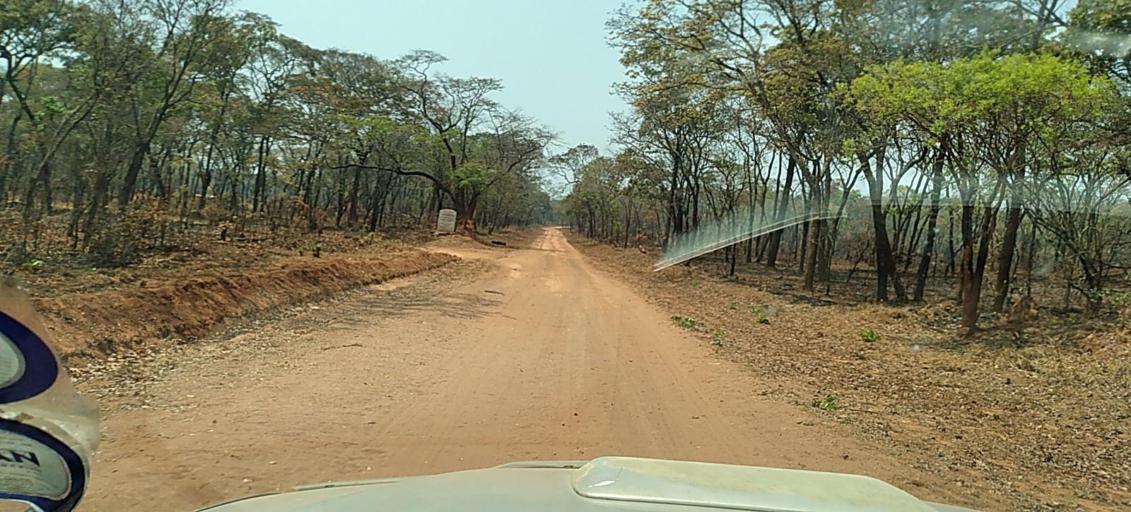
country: ZM
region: North-Western
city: Kasempa
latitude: -13.5482
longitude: 26.0559
